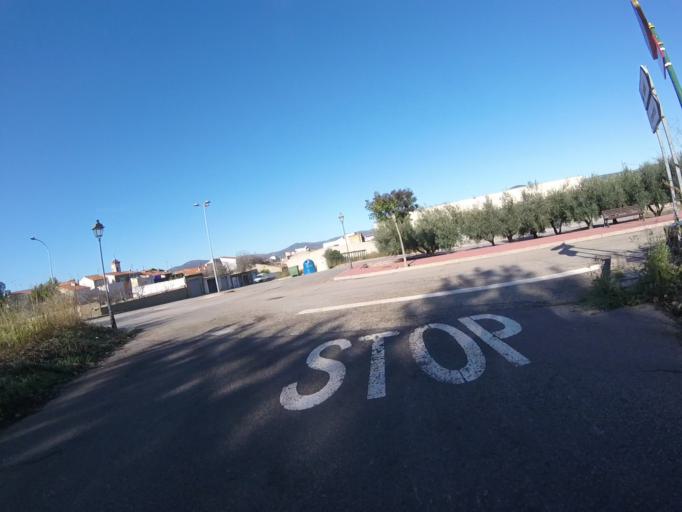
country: ES
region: Valencia
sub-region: Provincia de Castello
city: Santa Magdalena de Pulpis
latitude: 40.3559
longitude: 0.3051
